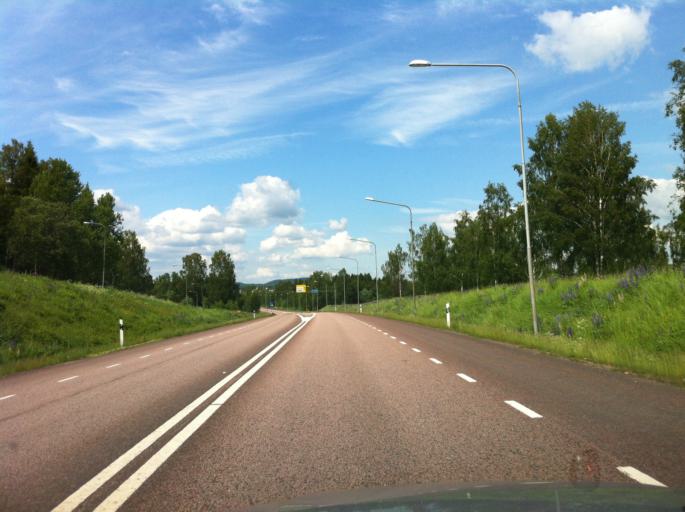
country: SE
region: Vaermland
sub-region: Sunne Kommun
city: Sunne
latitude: 59.8299
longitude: 13.1321
